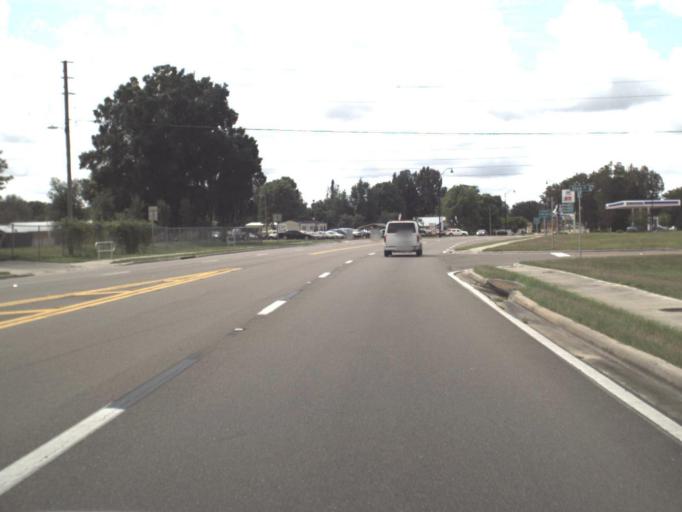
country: US
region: Florida
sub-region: Hardee County
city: Bowling Green
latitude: 27.6475
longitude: -81.8228
